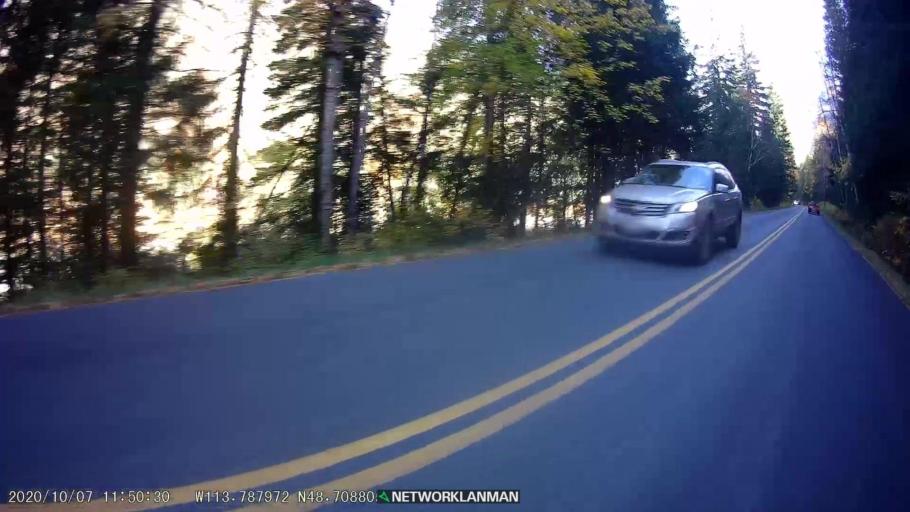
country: US
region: Montana
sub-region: Flathead County
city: Columbia Falls
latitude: 48.7091
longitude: -113.7878
